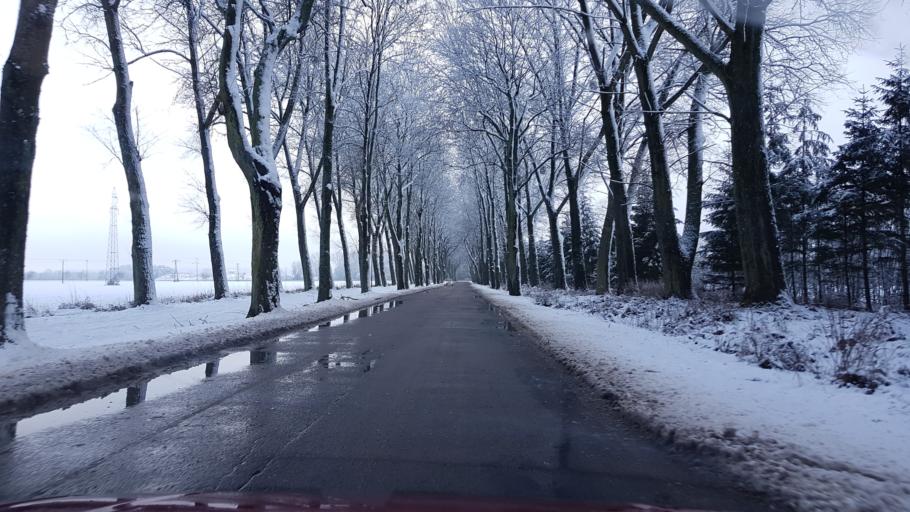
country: PL
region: West Pomeranian Voivodeship
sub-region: Powiat drawski
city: Zlocieniec
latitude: 53.5377
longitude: 16.0444
